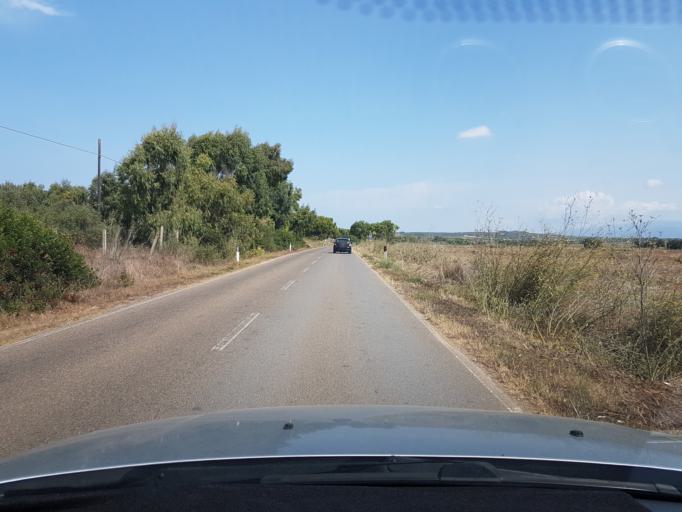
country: IT
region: Sardinia
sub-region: Provincia di Oristano
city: Cabras
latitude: 39.8943
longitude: 8.4348
